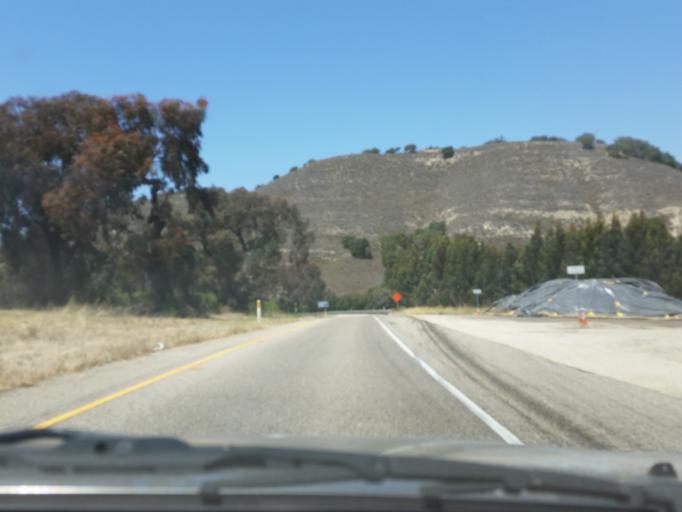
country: US
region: California
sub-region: San Luis Obispo County
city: Avila Beach
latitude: 35.1774
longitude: -120.6976
